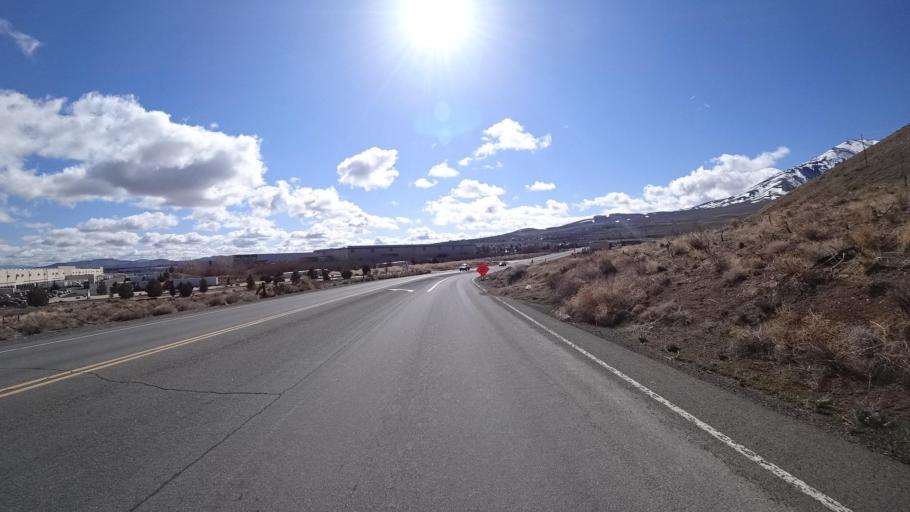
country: US
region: Nevada
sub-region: Washoe County
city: Cold Springs
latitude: 39.6357
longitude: -119.9195
